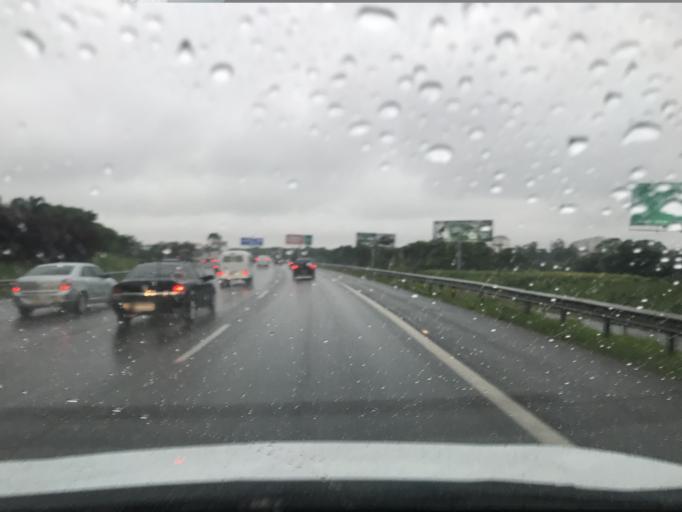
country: BR
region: Sao Paulo
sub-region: Guarulhos
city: Guarulhos
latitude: -23.4960
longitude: -46.5429
